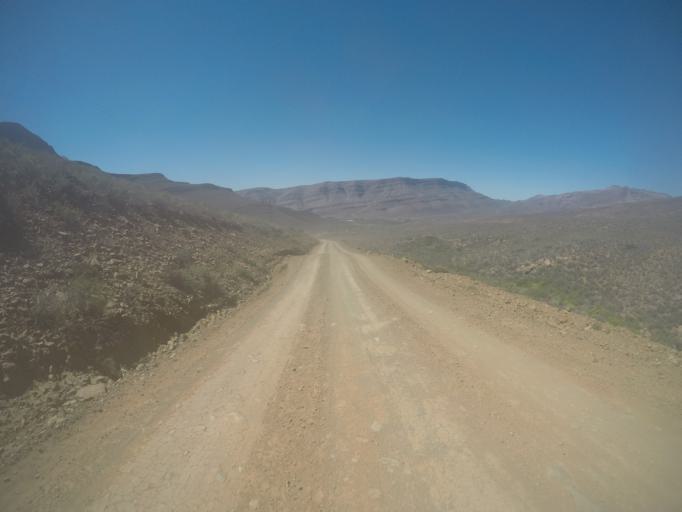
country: ZA
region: Western Cape
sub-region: West Coast District Municipality
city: Clanwilliam
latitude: -32.6177
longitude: 19.3774
